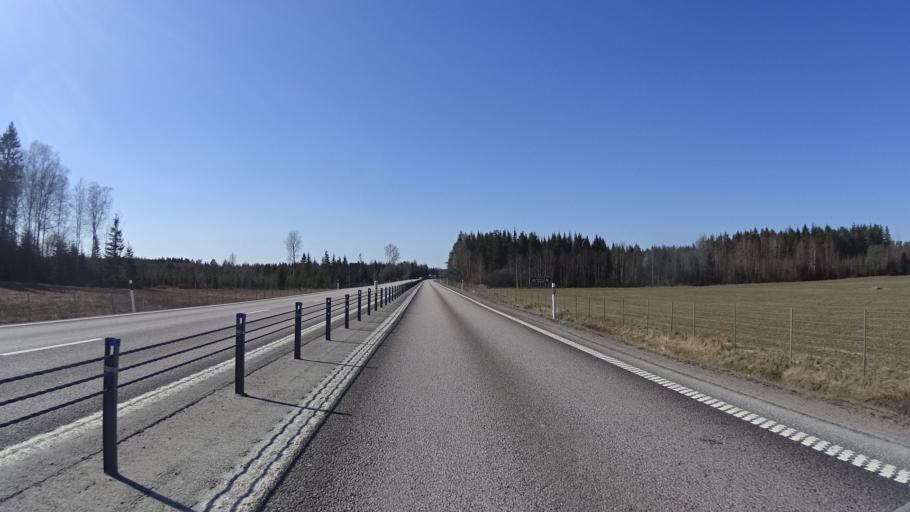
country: SE
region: Vaermland
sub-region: Karlstads Kommun
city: Skattkarr
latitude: 59.3917
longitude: 13.8407
